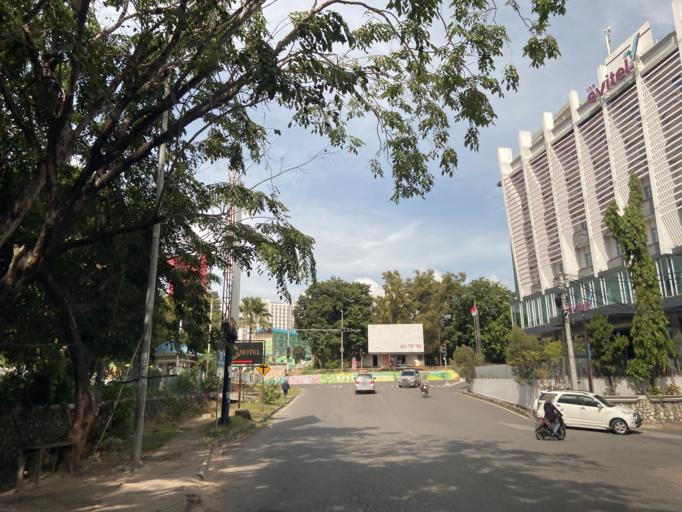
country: SG
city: Singapore
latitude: 1.1474
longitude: 104.0170
